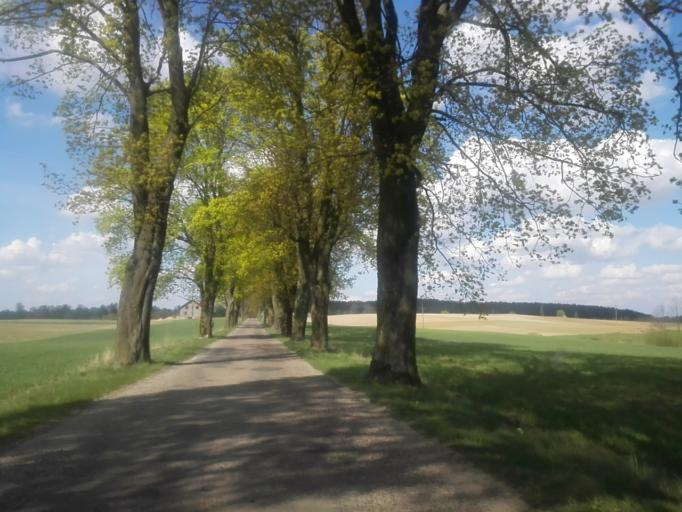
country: PL
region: Kujawsko-Pomorskie
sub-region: Powiat brodnicki
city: Bartniczka
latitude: 53.2798
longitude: 19.6898
